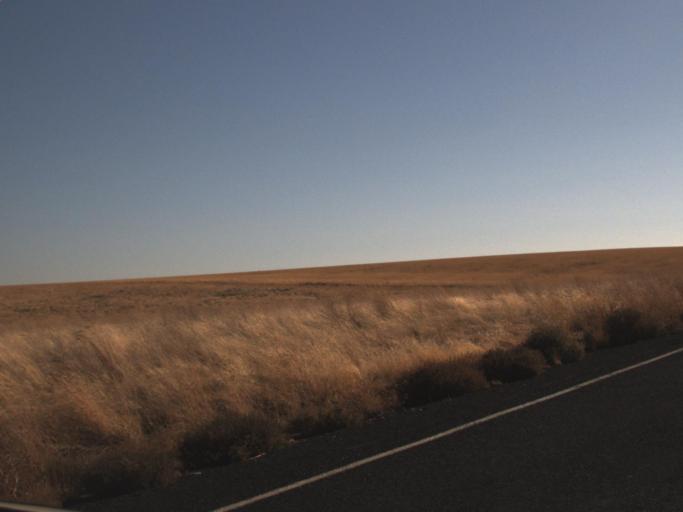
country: US
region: Washington
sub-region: Adams County
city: Ritzville
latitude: 47.0456
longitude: -118.6631
